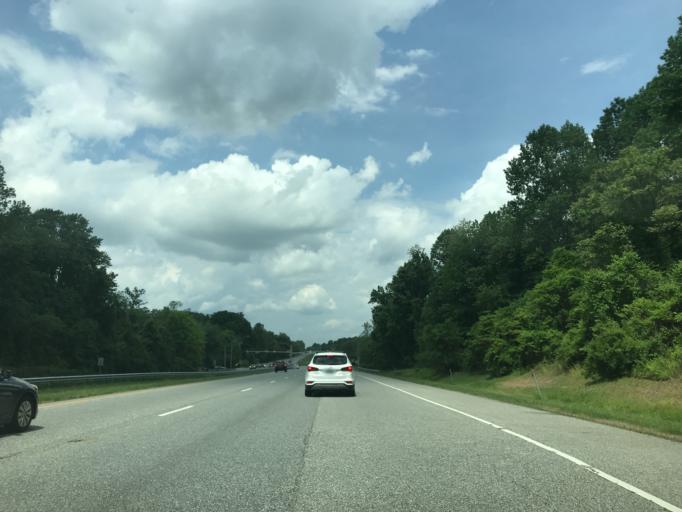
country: US
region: Maryland
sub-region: Harford County
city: Bel Air South
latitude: 39.4903
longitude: -76.3253
